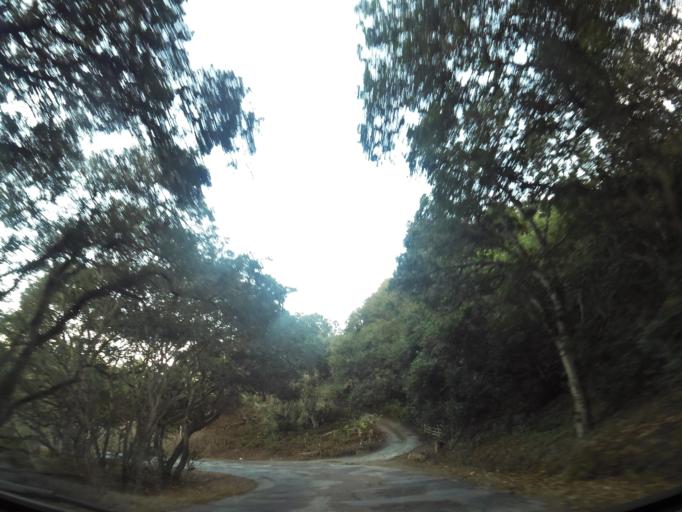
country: US
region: California
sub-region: San Benito County
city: San Juan Bautista
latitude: 36.8329
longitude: -121.5683
